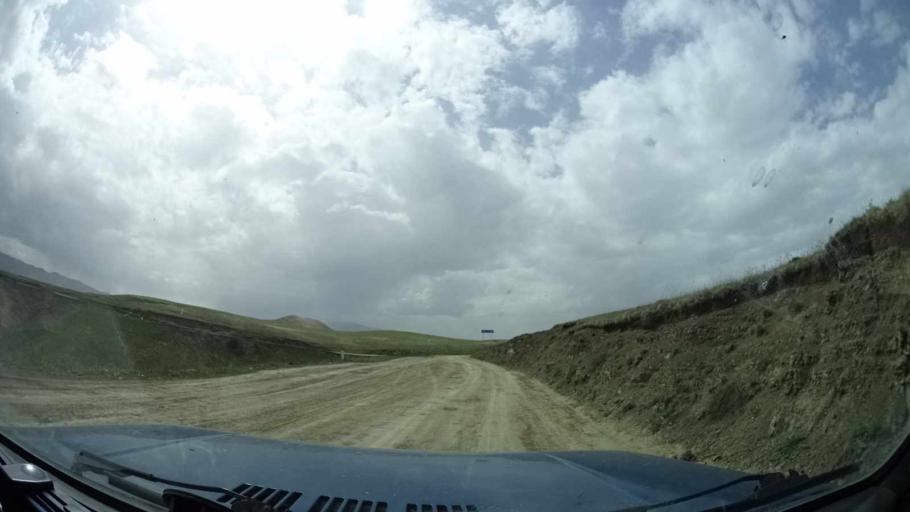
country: RU
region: Dagestan
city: Kubachi
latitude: 42.0838
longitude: 47.5593
